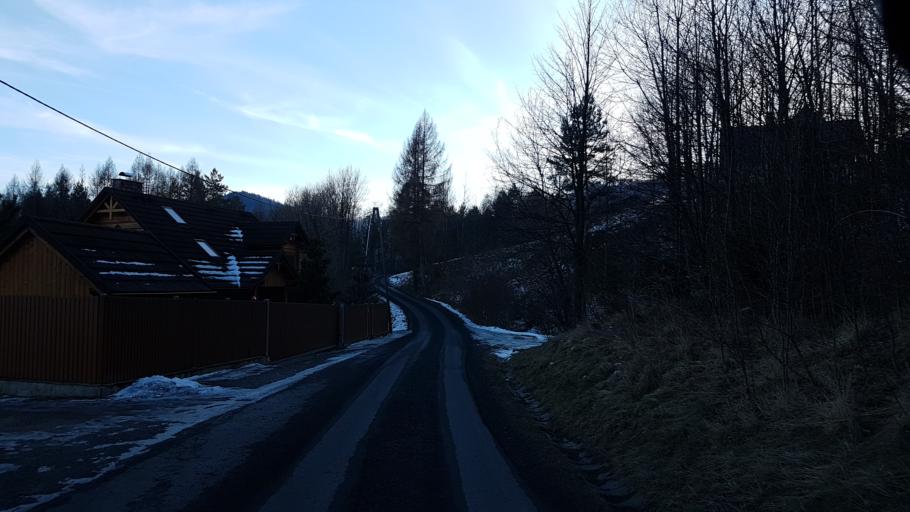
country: PL
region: Lesser Poland Voivodeship
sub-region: Powiat nowosadecki
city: Rytro
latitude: 49.4907
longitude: 20.6572
